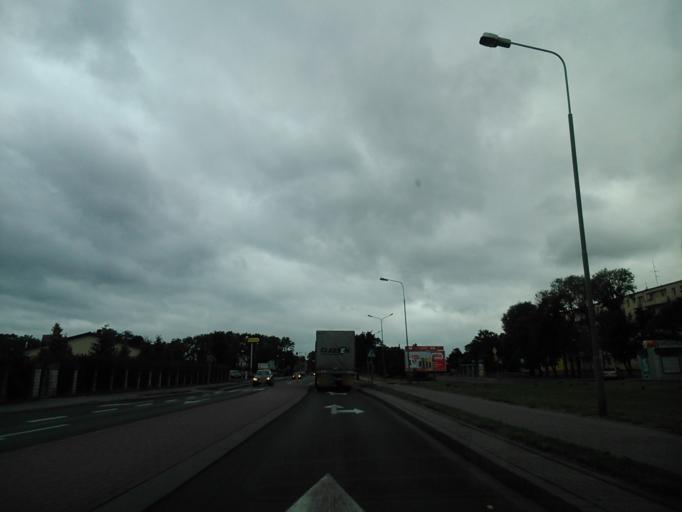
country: PL
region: Kujawsko-Pomorskie
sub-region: Powiat inowroclawski
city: Kruszwica
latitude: 52.6743
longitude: 18.3347
